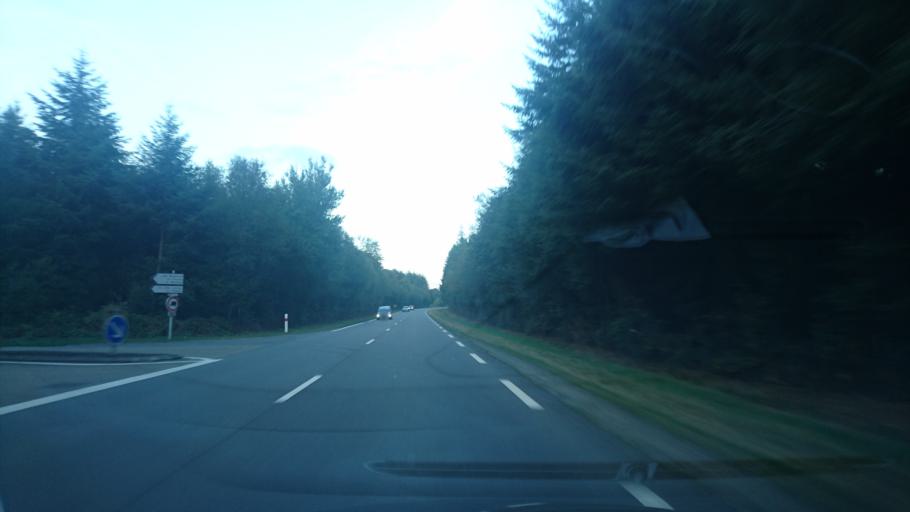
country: FR
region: Brittany
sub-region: Departement d'Ille-et-Vilaine
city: Baulon
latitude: 47.9349
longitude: -1.9372
